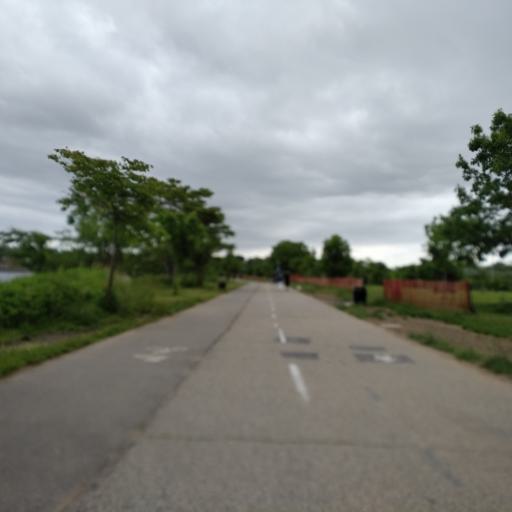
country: US
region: New York
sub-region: Nassau County
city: East Atlantic Beach
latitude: 40.7902
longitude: -73.7884
